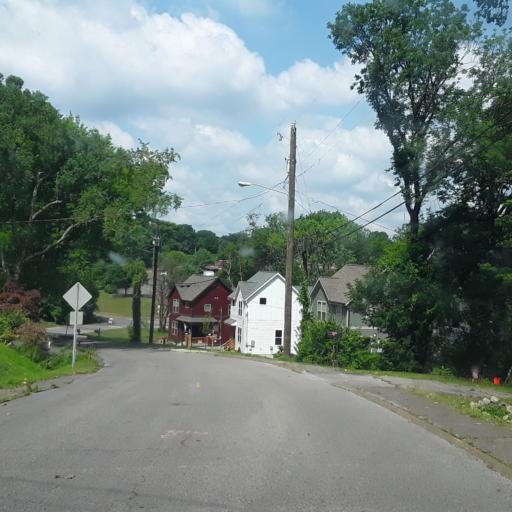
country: US
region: Tennessee
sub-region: Davidson County
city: Oak Hill
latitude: 36.1154
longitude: -86.7334
